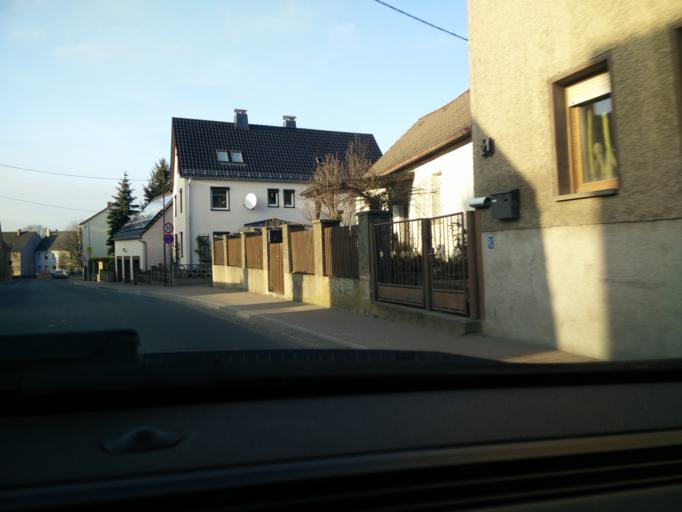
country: DE
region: Saxony
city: Otterwisch
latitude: 51.2523
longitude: 12.6417
